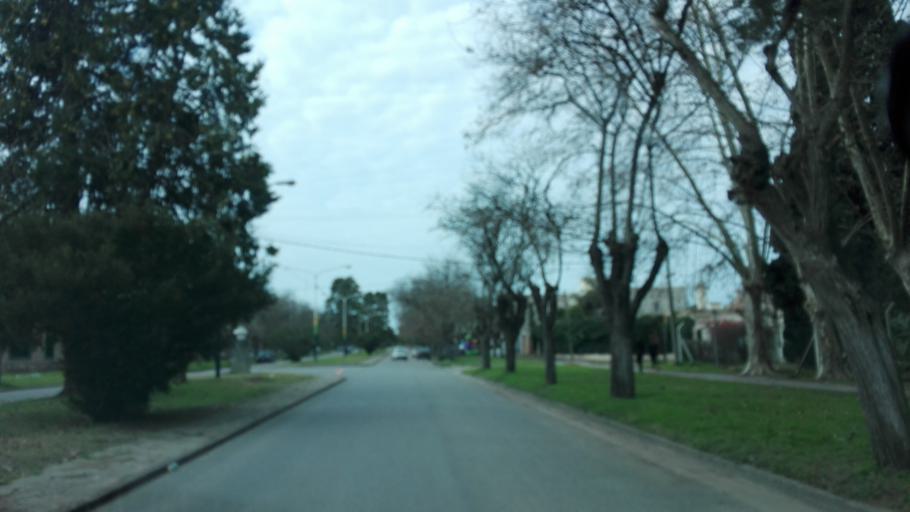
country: AR
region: Buenos Aires
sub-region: Partido de Chascomus
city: Chascomus
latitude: -35.5782
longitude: -58.0177
